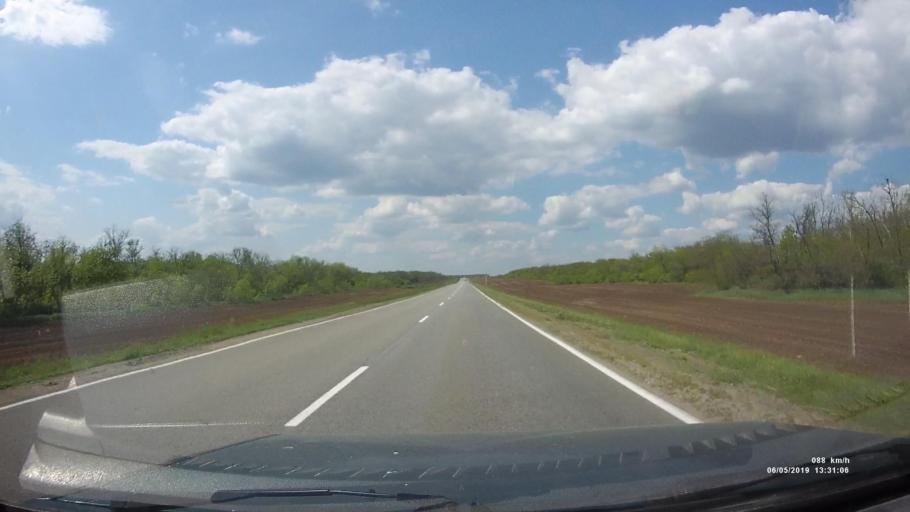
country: RU
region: Rostov
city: Ust'-Donetskiy
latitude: 47.6739
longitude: 40.8163
